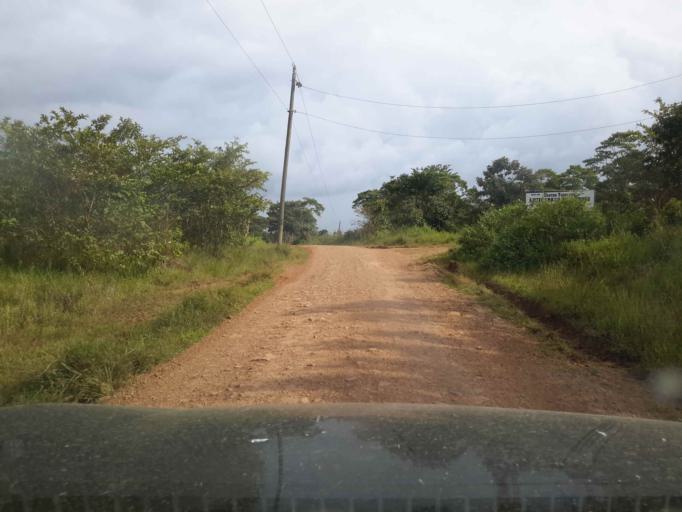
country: CR
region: Alajuela
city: Los Chiles
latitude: 11.0841
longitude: -84.5388
